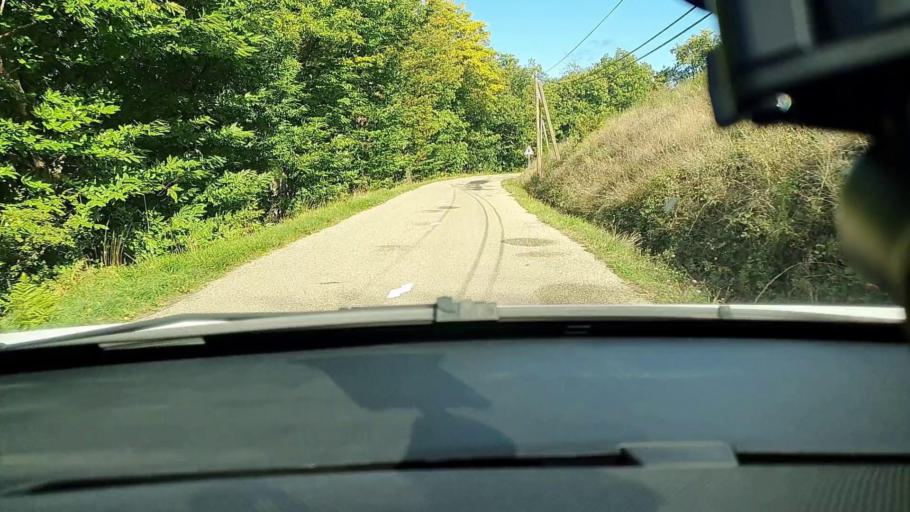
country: FR
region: Rhone-Alpes
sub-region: Departement de l'Ardeche
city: Les Vans
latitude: 44.4173
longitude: 4.0214
